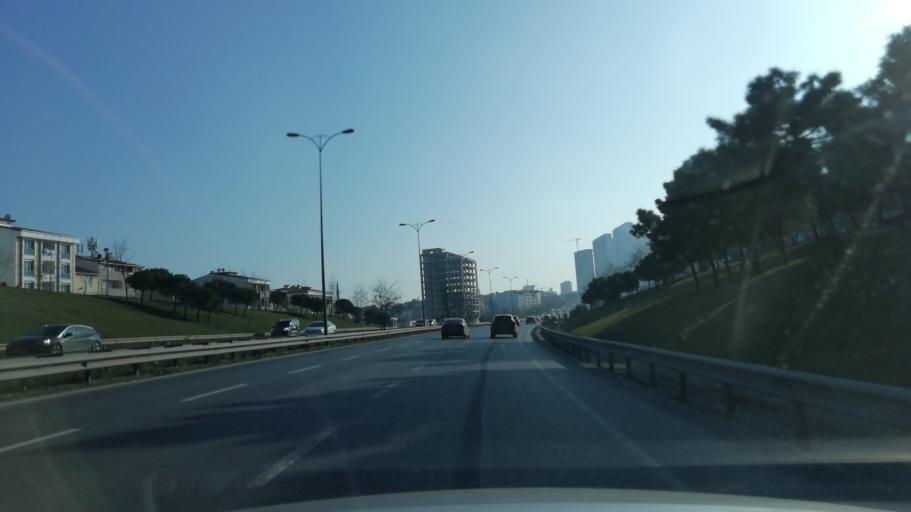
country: TR
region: Istanbul
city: Esenyurt
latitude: 41.0434
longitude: 28.6907
